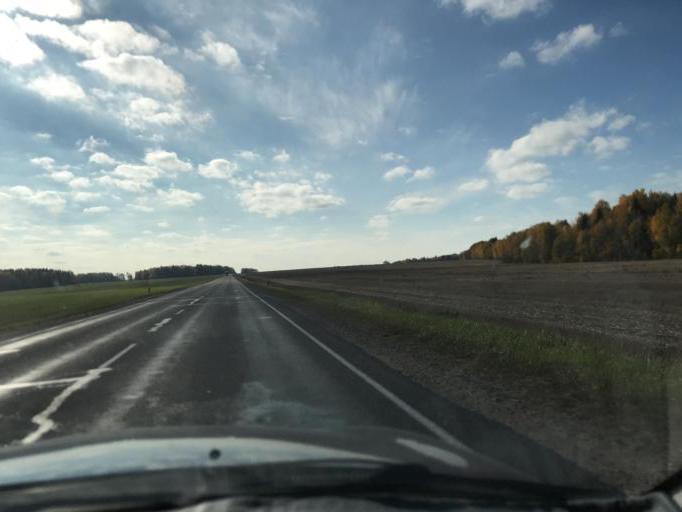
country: BY
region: Grodnenskaya
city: Voranava
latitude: 54.1999
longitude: 25.3474
